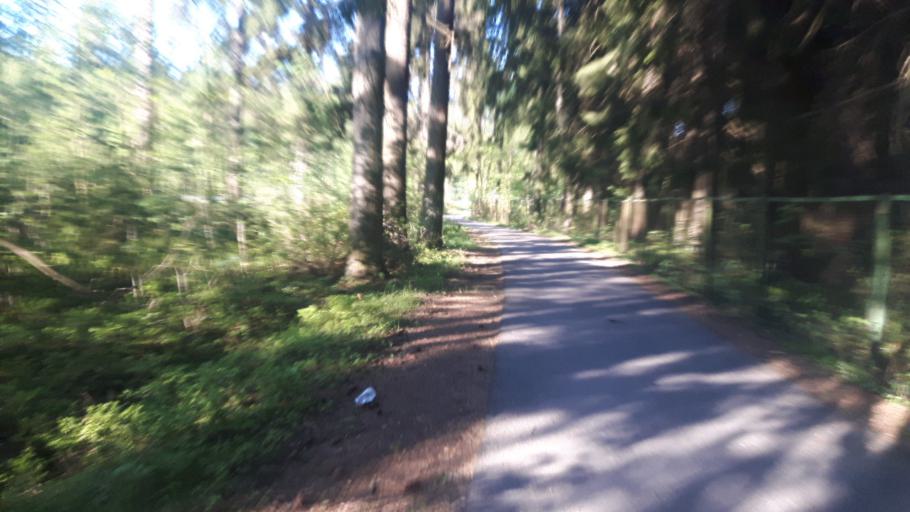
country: RU
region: Leningrad
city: Molodezhnoye
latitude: 60.1814
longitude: 29.4985
